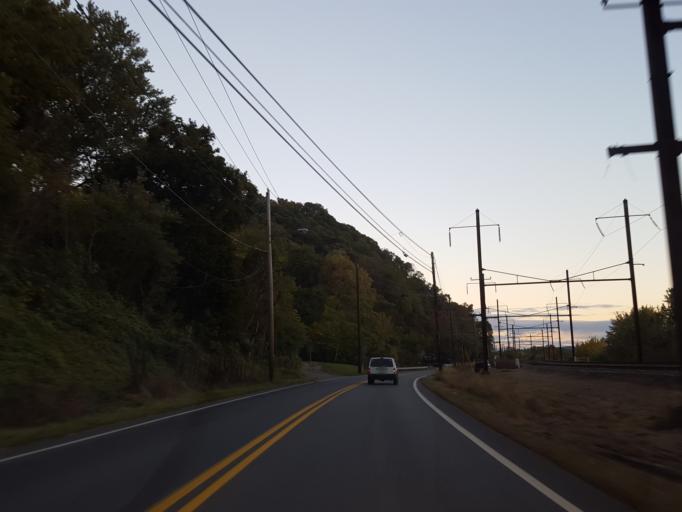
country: US
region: Pennsylvania
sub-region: Lancaster County
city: Columbia
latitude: 40.0229
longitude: -76.4924
